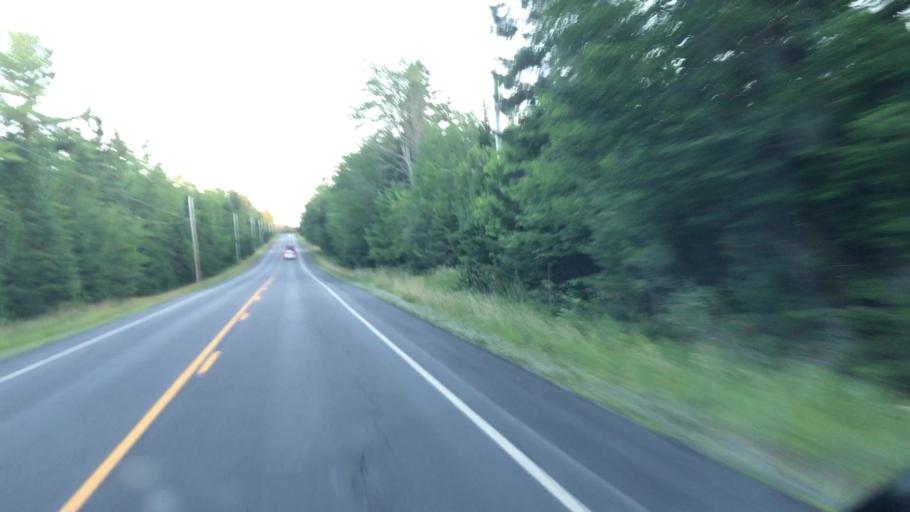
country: US
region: Maine
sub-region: Penobscot County
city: Medway
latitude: 45.5760
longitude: -68.3198
